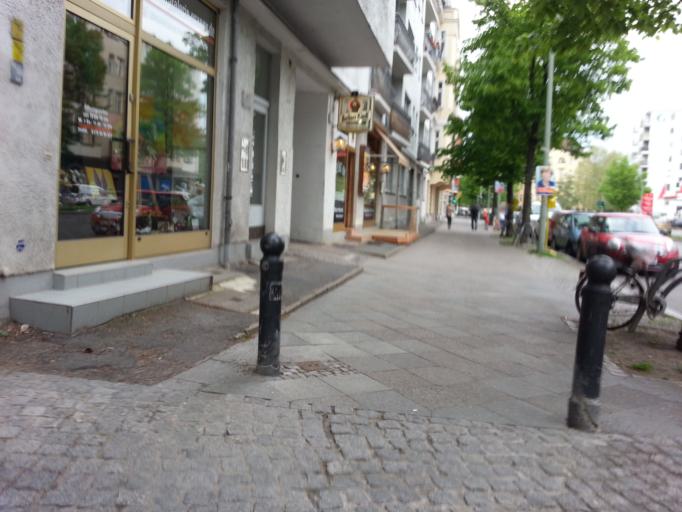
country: DE
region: Berlin
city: Charlottenburg-Nord
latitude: 52.5164
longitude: 13.3005
